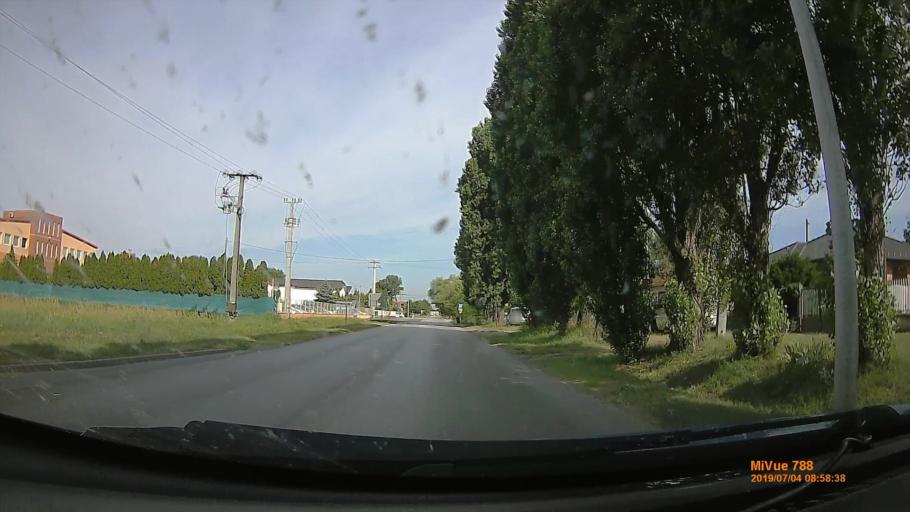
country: HU
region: Pest
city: Gyal
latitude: 47.4011
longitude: 19.2483
